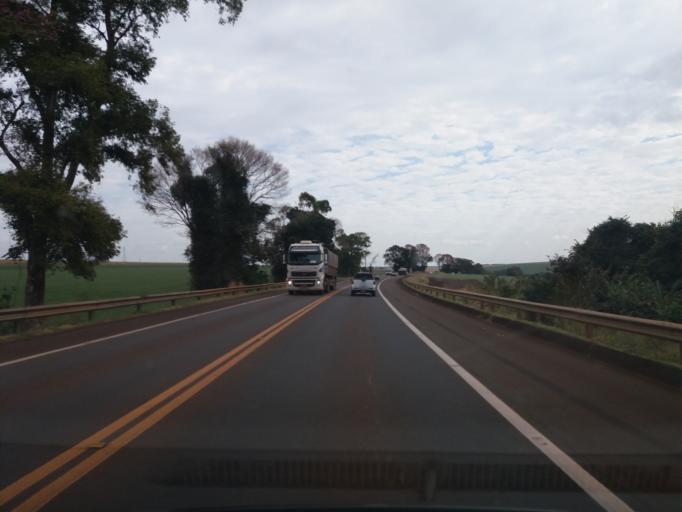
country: BR
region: Parana
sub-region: Campo Mourao
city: Campo Mourao
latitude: -24.3188
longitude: -52.6269
